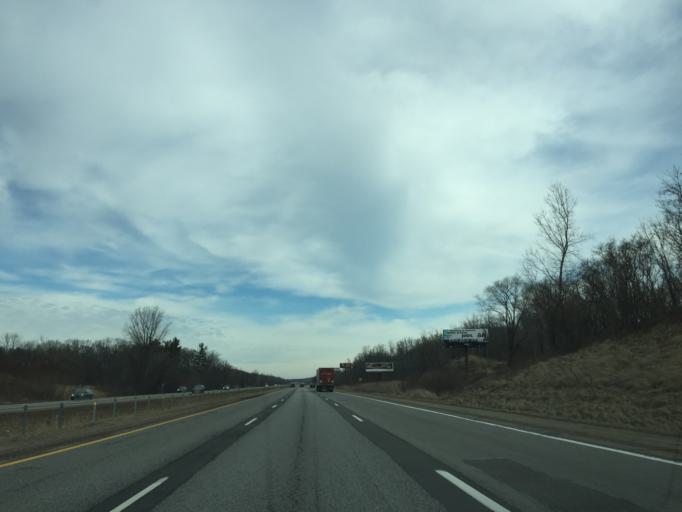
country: US
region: Michigan
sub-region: Berrien County
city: Bridgman
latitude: 41.9811
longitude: -86.5430
